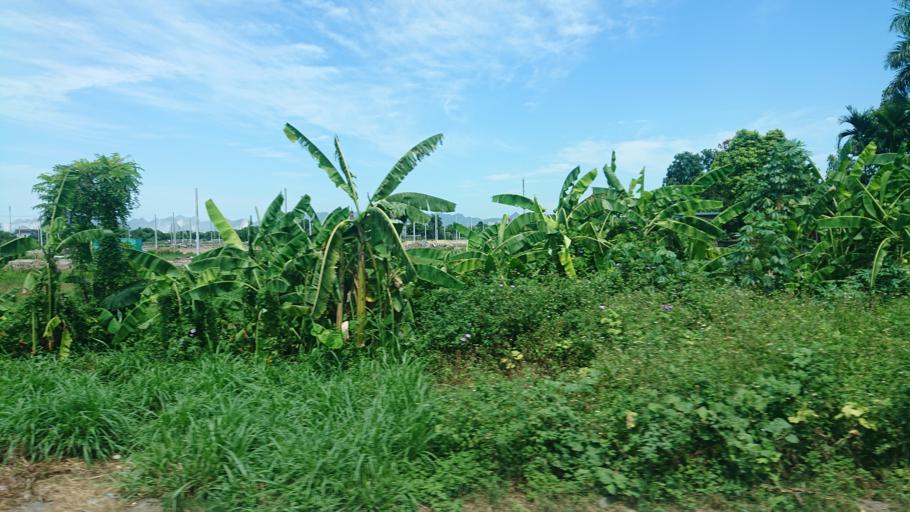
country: VN
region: Ha Nam
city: Thanh Pho Phu Ly
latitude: 20.5350
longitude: 105.9454
